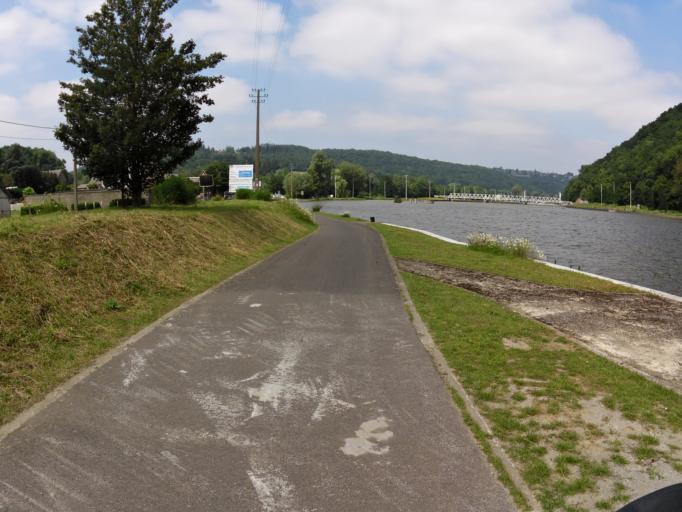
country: BE
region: Wallonia
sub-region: Province de Namur
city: Hastiere-Lavaux
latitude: 50.1969
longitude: 4.8206
